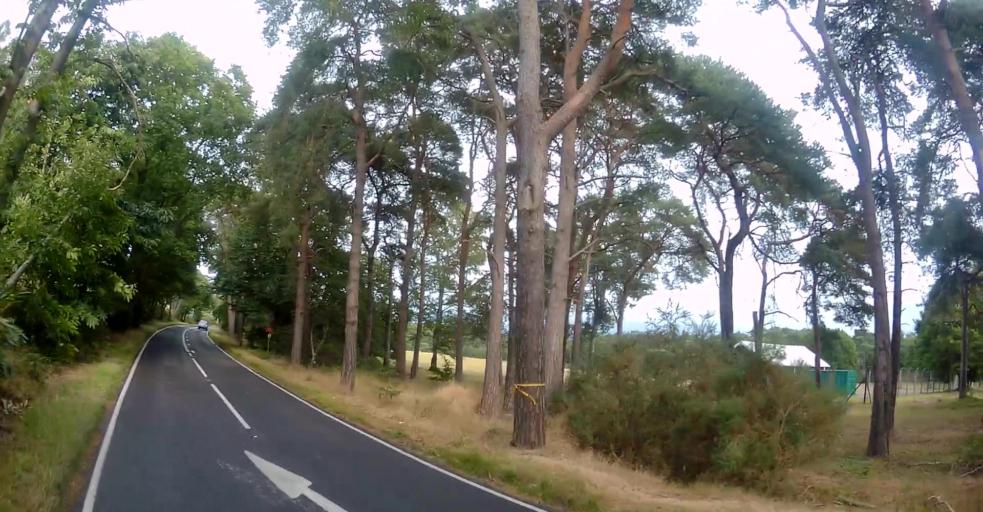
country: GB
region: England
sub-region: Surrey
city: Pirbright
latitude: 51.2990
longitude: -0.6764
